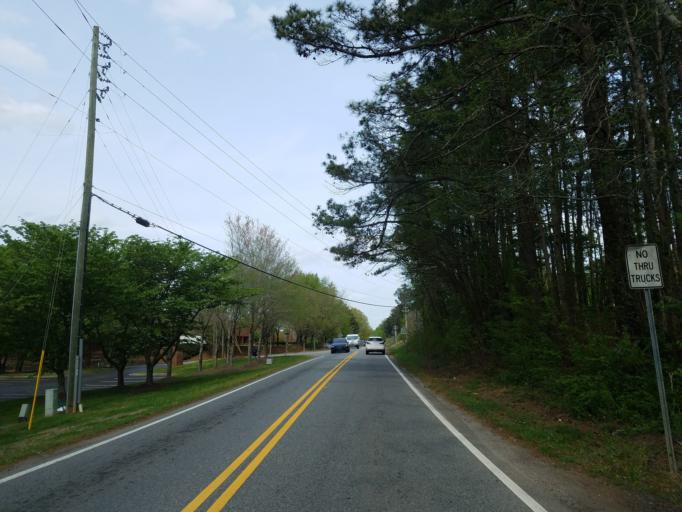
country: US
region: Georgia
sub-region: Fulton County
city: Johns Creek
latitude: 34.0992
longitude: -84.2139
